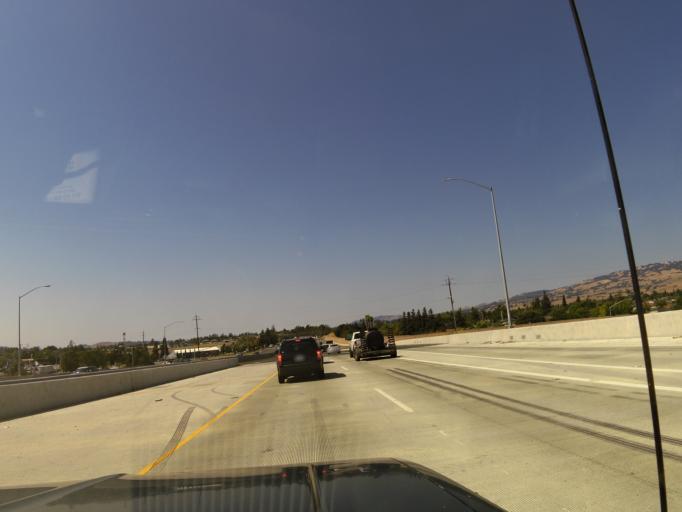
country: US
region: California
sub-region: Sonoma County
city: Petaluma
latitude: 38.2330
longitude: -122.6176
